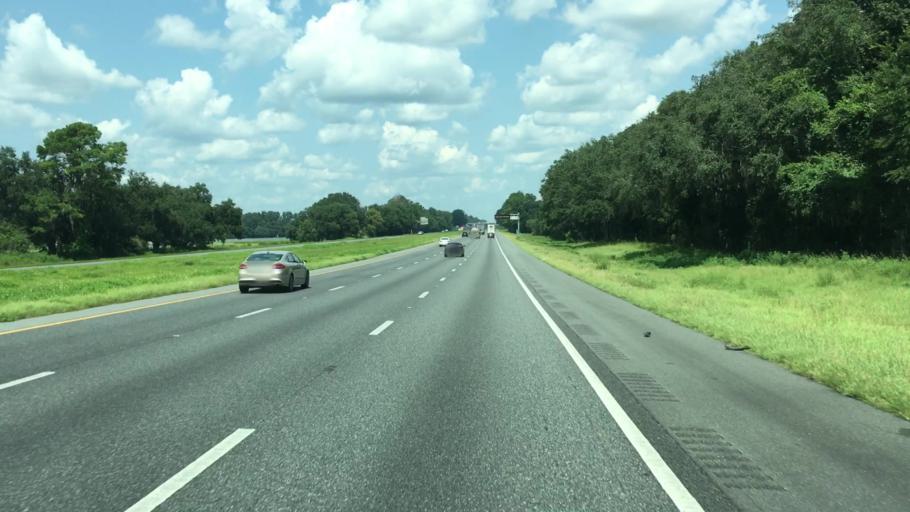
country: US
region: Florida
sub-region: Suwannee County
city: Wellborn
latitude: 30.2805
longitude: -82.7638
